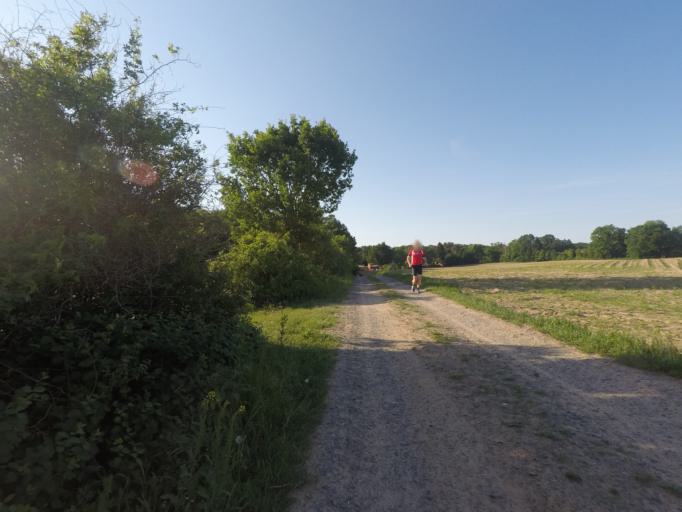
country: DE
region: Brandenburg
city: Joachimsthal
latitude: 52.9028
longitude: 13.7023
